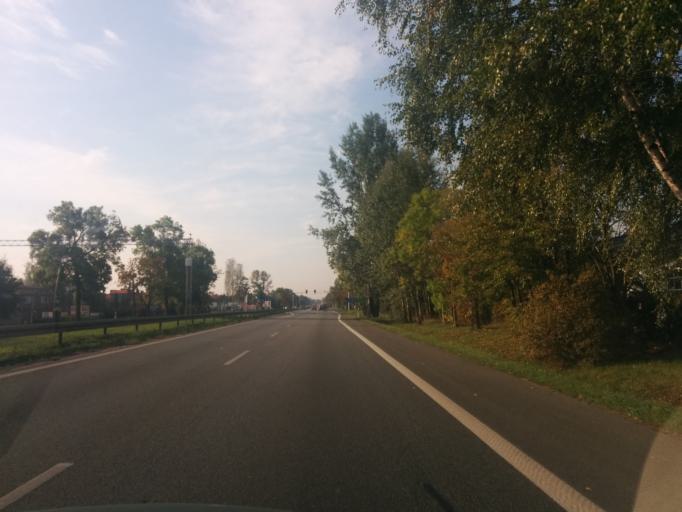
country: PL
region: Masovian Voivodeship
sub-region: Powiat piaseczynski
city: Tarczyn
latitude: 52.0409
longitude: 20.8619
